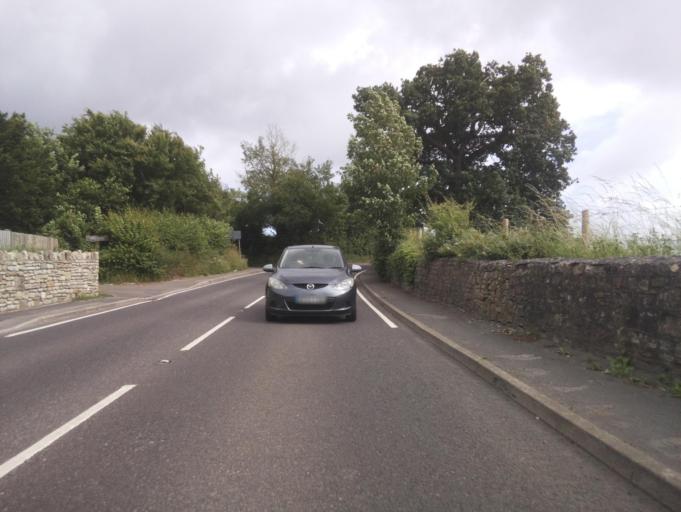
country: GB
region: England
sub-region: Bath and North East Somerset
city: Corston
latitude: 51.4015
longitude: -2.4288
